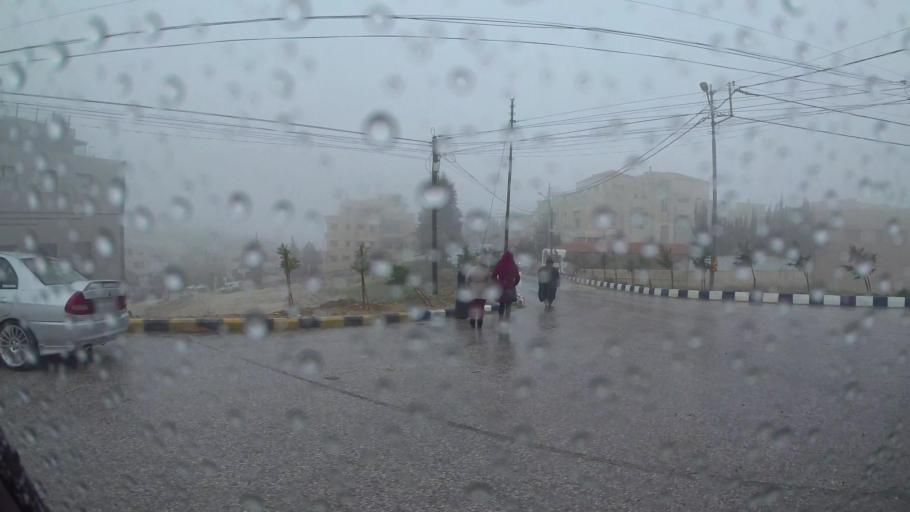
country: JO
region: Amman
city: Wadi as Sir
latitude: 31.9978
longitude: 35.8206
